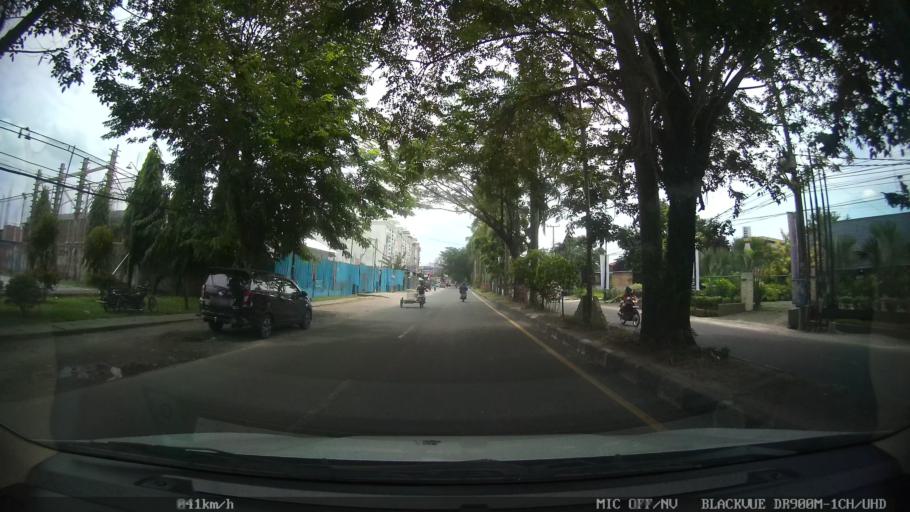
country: ID
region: North Sumatra
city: Sunggal
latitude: 3.5247
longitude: 98.6297
